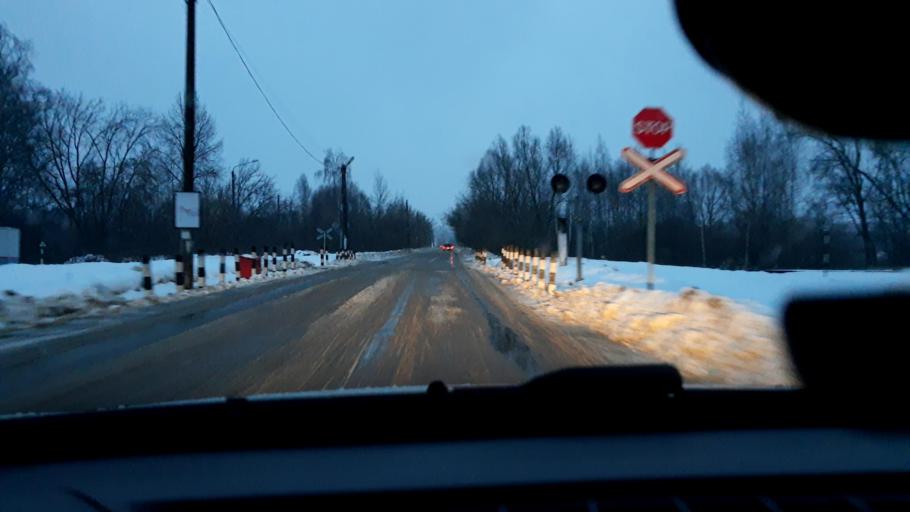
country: RU
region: Nizjnij Novgorod
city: Bogorodsk
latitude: 56.1115
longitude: 43.4860
